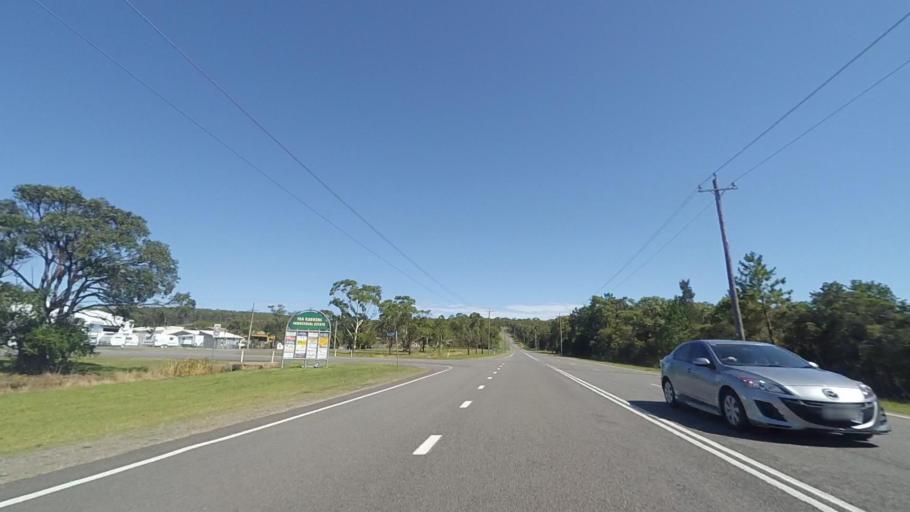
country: AU
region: New South Wales
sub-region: Great Lakes
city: Hawks Nest
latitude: -32.6457
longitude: 152.1469
